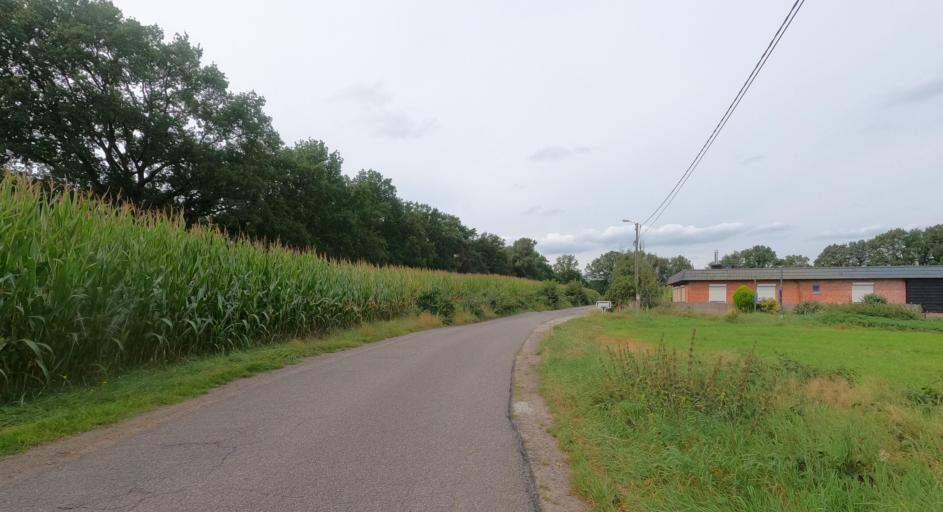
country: BE
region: Flanders
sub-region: Provincie Antwerpen
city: Essen
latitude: 51.4595
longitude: 4.5079
